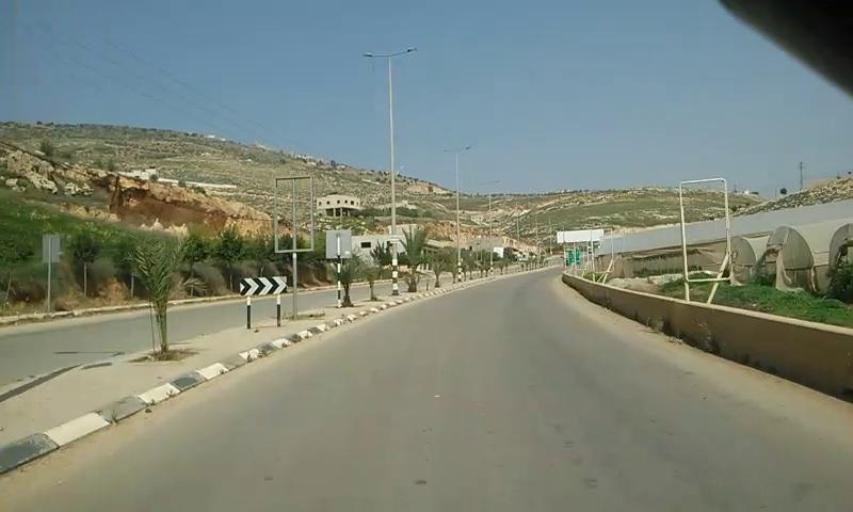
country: PS
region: West Bank
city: Tubas
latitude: 32.3064
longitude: 35.3639
